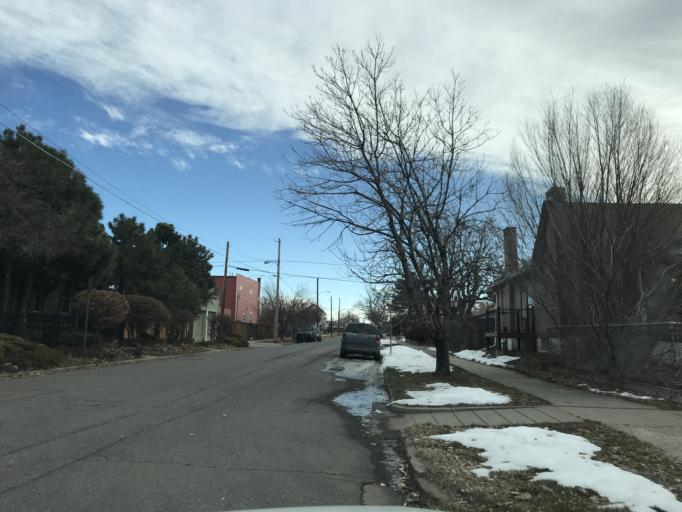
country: US
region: Colorado
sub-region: Denver County
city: Denver
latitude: 39.7682
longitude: -104.9635
